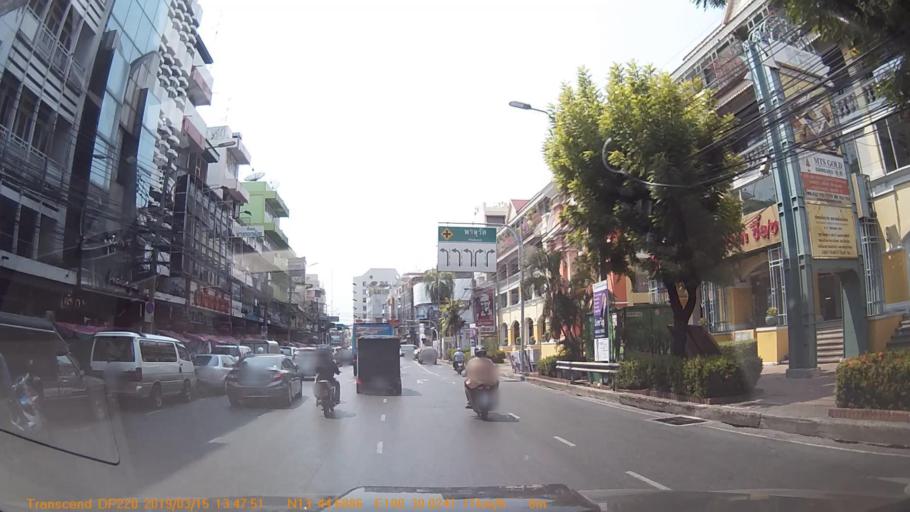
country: TH
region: Bangkok
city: Bangkok
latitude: 13.7448
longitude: 100.5004
